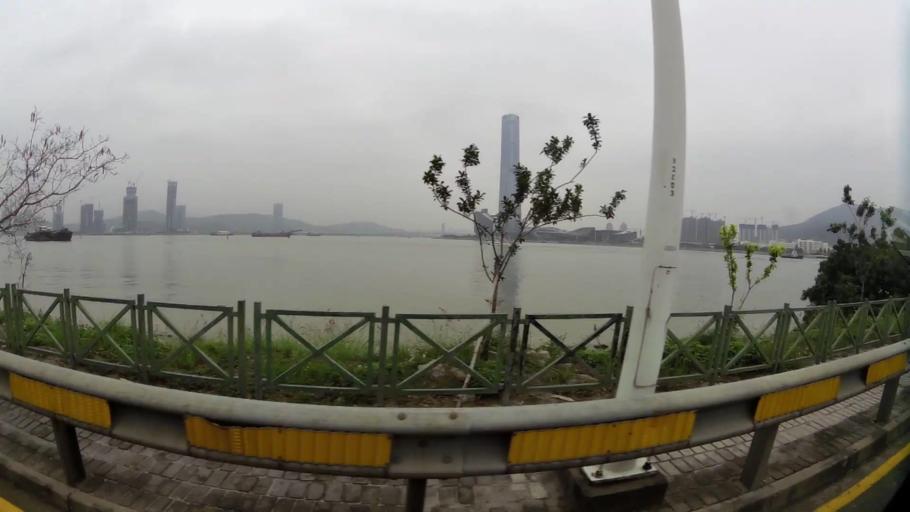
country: CN
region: Guangdong
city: Wanzai
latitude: 22.1808
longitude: 113.5305
